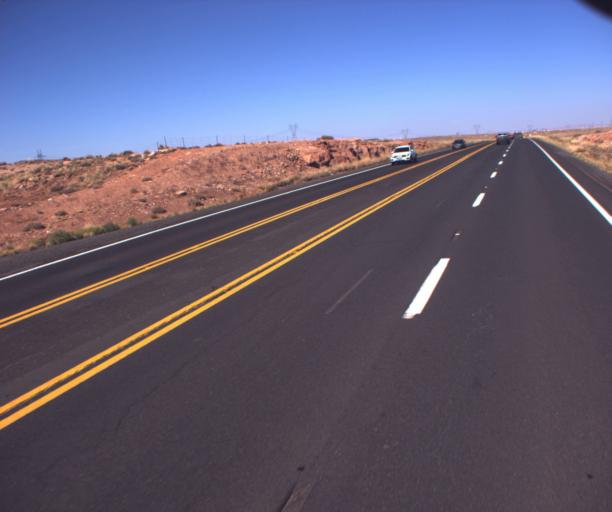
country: US
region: Arizona
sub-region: Coconino County
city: Tuba City
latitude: 35.7982
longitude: -111.4472
